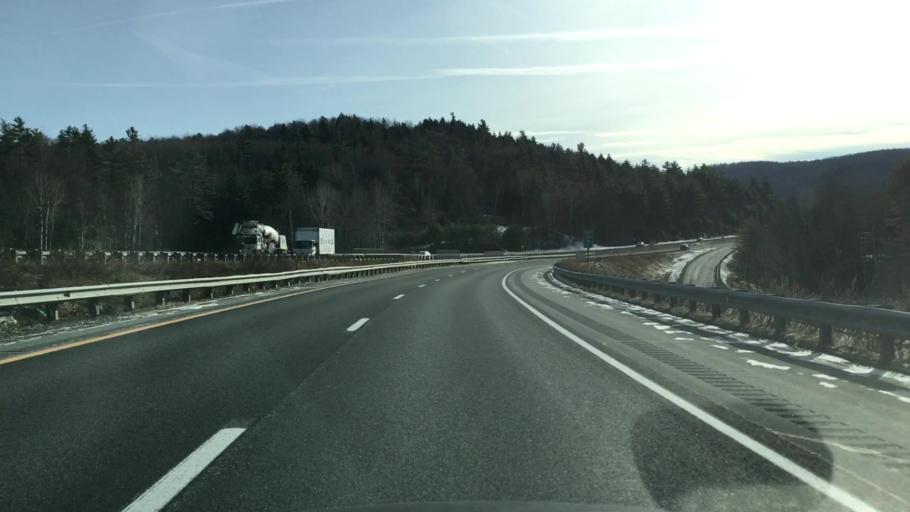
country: US
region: New Hampshire
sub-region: Grafton County
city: Enfield
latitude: 43.5984
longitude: -72.1660
